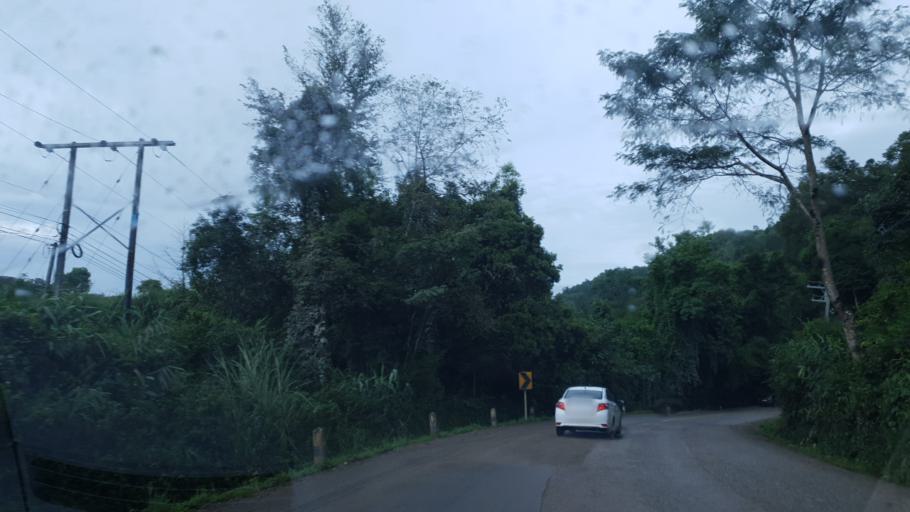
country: TH
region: Mae Hong Son
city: Ban Huai I Huak
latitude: 18.1503
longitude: 98.1414
